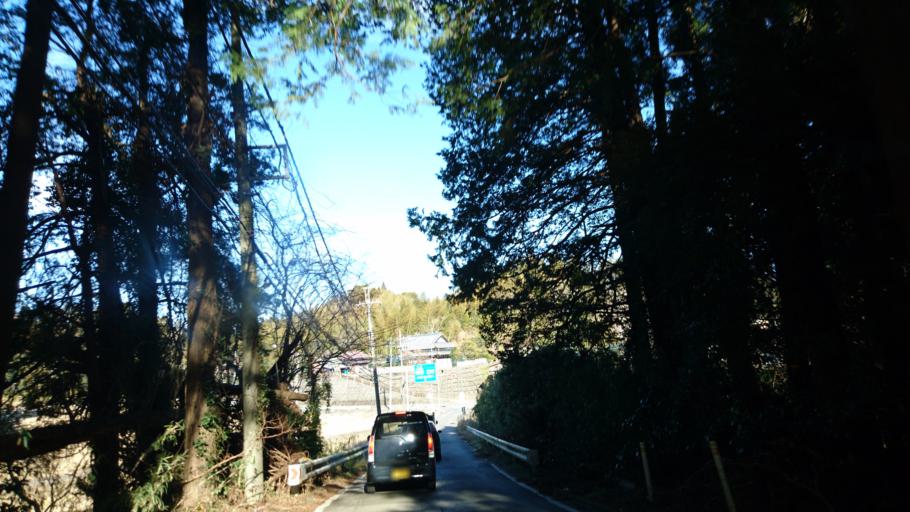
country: JP
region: Chiba
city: Yachimata
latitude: 35.6152
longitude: 140.3365
